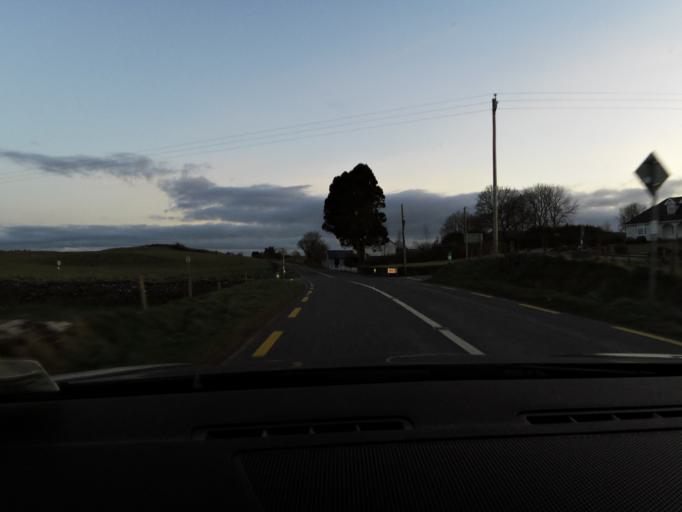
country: IE
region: Connaught
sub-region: Roscommon
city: Boyle
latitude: 53.8802
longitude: -8.2475
